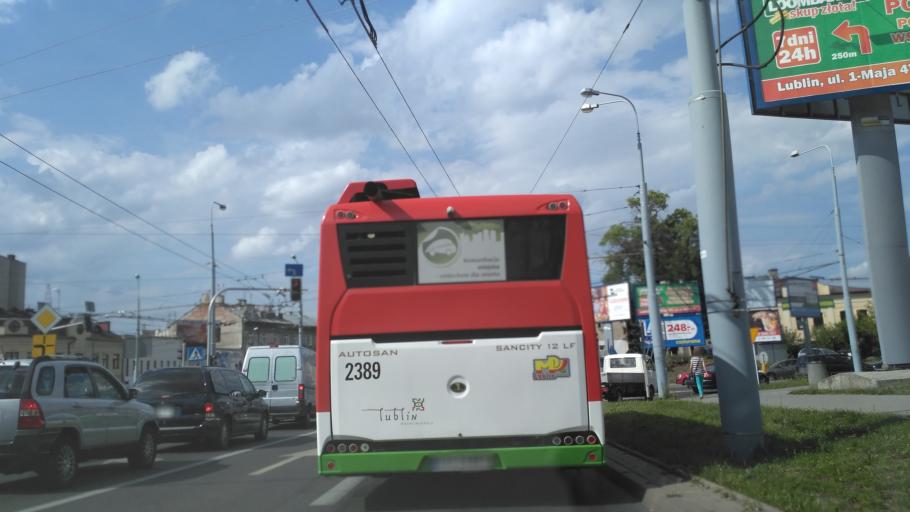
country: PL
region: Lublin Voivodeship
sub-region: Powiat lubelski
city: Lublin
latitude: 51.2340
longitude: 22.5711
